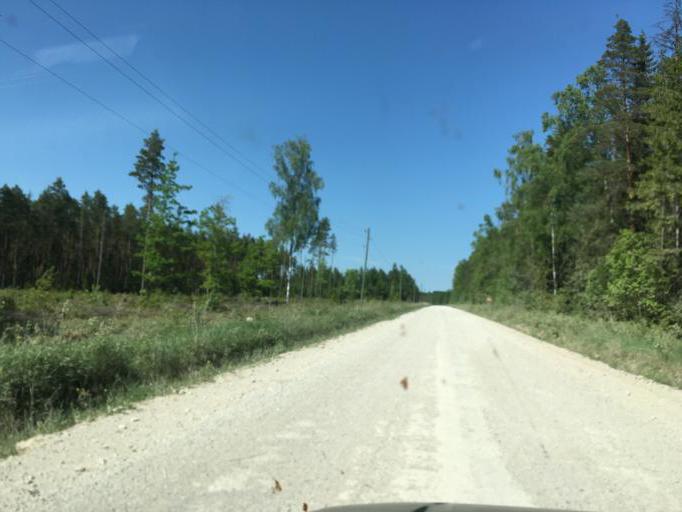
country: LV
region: Dundaga
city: Dundaga
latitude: 57.4427
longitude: 22.3196
